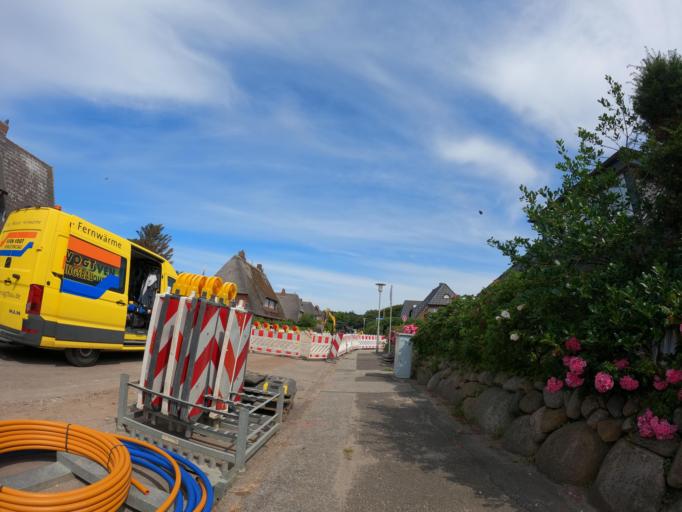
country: DE
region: Schleswig-Holstein
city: Westerland
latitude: 54.9176
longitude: 8.3112
